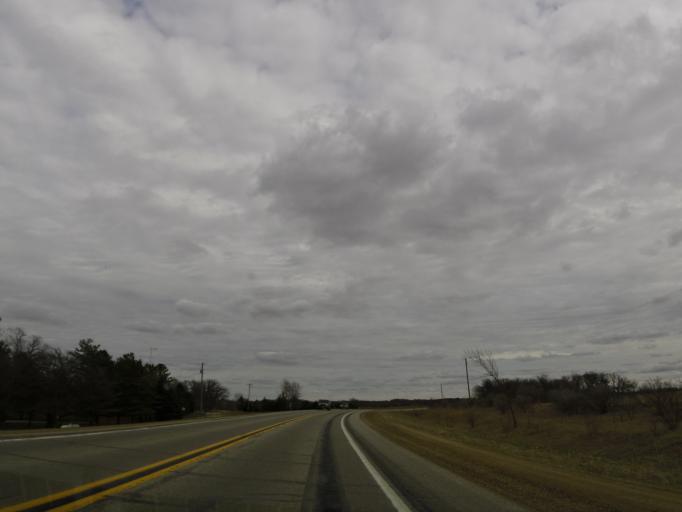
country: US
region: Minnesota
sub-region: Fillmore County
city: Spring Valley
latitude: 43.4718
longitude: -92.3226
